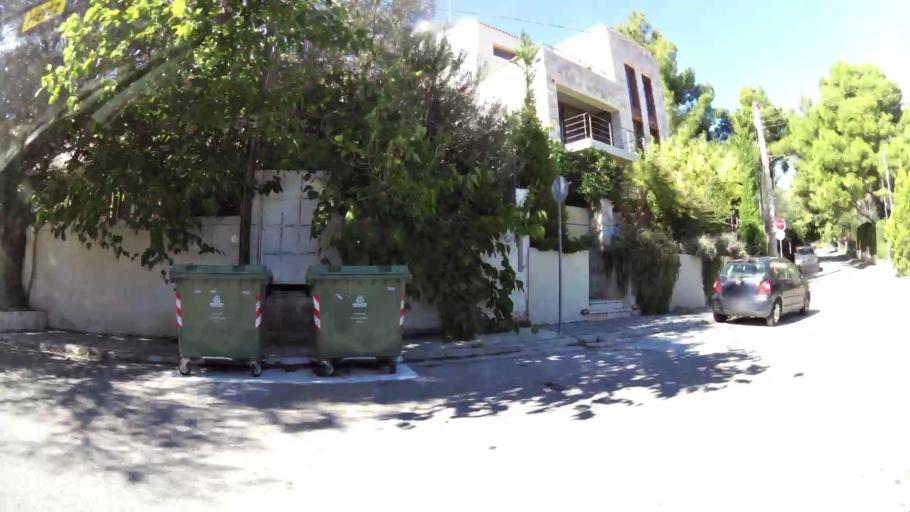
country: GR
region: Attica
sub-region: Nomarchia Anatolikis Attikis
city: Leondarion
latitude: 37.9831
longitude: 23.8596
